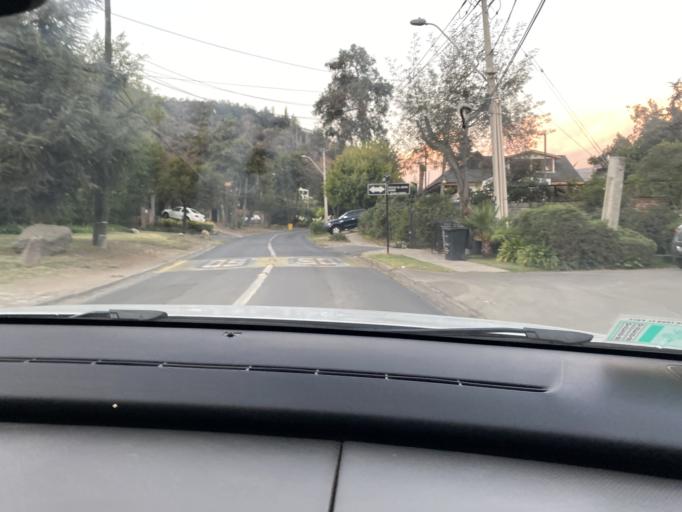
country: CL
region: Santiago Metropolitan
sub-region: Provincia de Santiago
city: Villa Presidente Frei, Nunoa, Santiago, Chile
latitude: -33.3583
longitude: -70.4838
